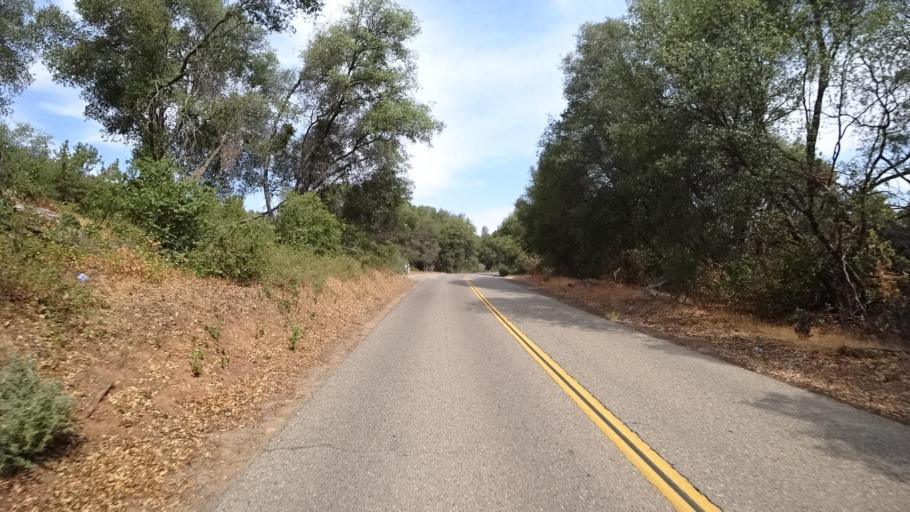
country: US
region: California
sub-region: Mariposa County
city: Midpines
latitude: 37.4917
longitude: -119.9091
